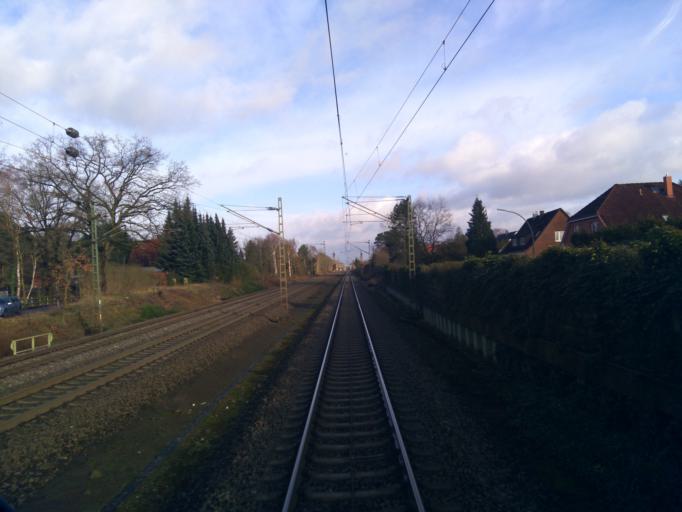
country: DE
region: Lower Saxony
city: Rotenburg
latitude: 53.1197
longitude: 9.4146
